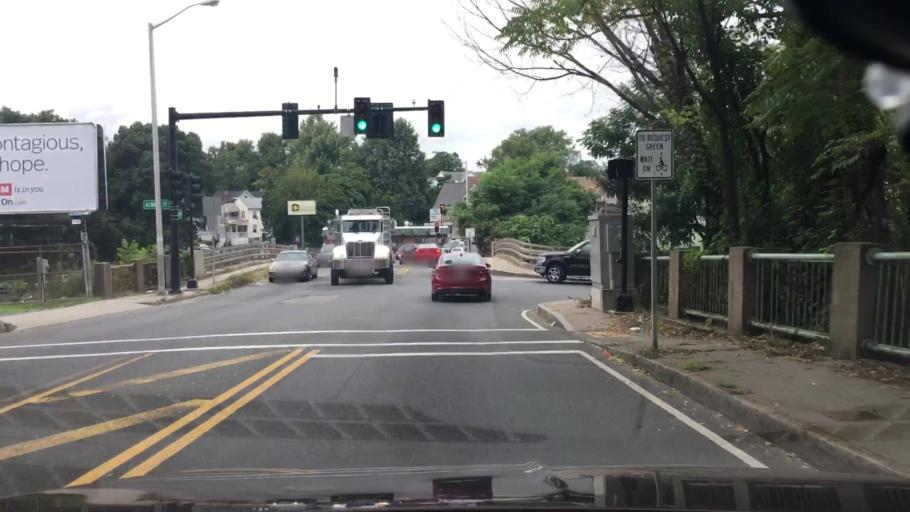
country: US
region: Massachusetts
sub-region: Hampden County
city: Springfield
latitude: 42.1152
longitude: -72.5814
